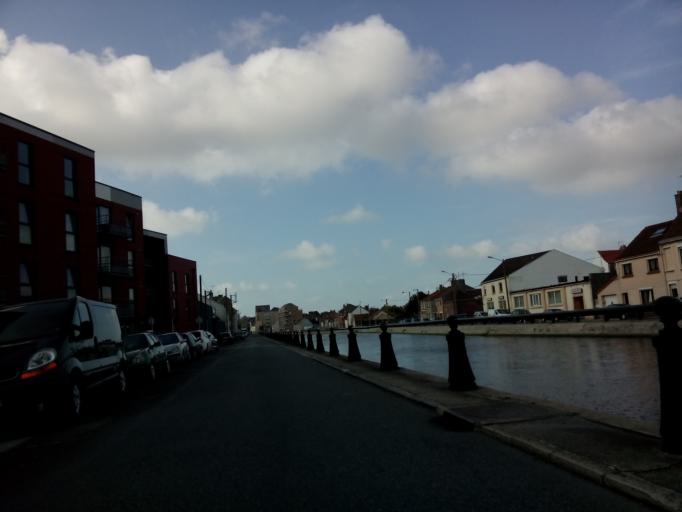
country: FR
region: Nord-Pas-de-Calais
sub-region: Departement du Pas-de-Calais
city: Calais
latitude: 50.9409
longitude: 1.8697
